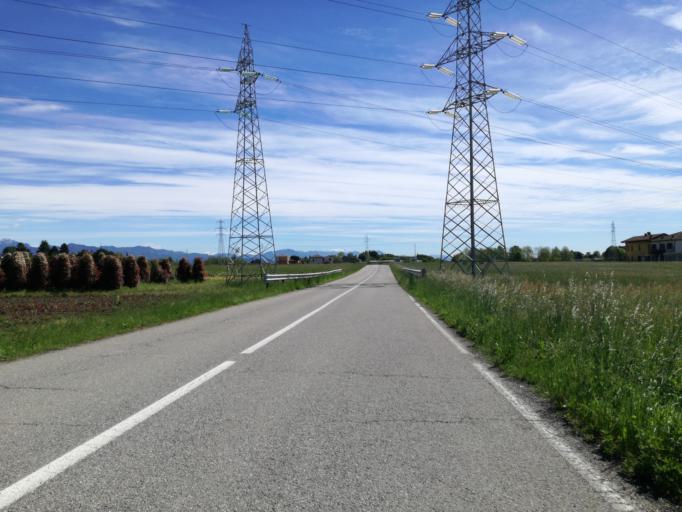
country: IT
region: Lombardy
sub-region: Provincia di Monza e Brianza
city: Porto d'Adda
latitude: 45.6614
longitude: 9.4631
